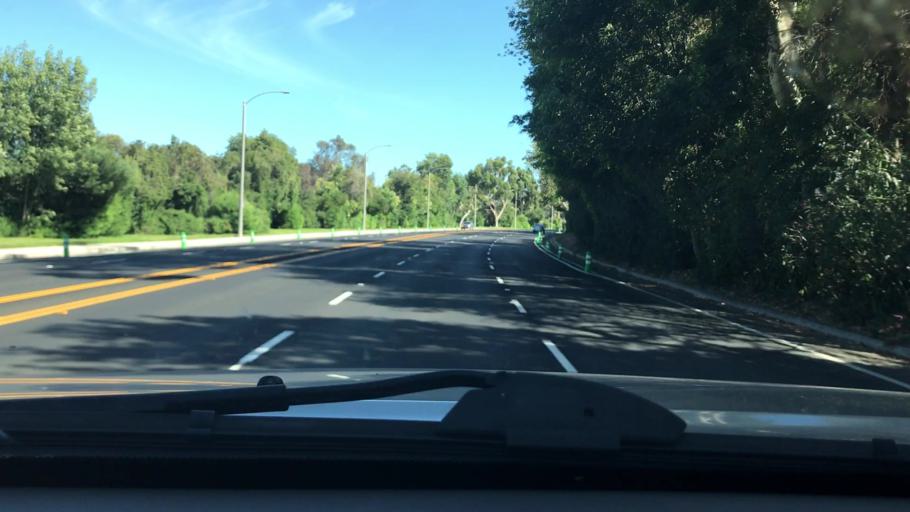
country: US
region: California
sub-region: Orange County
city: Rossmoor
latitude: 33.7866
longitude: -118.1232
